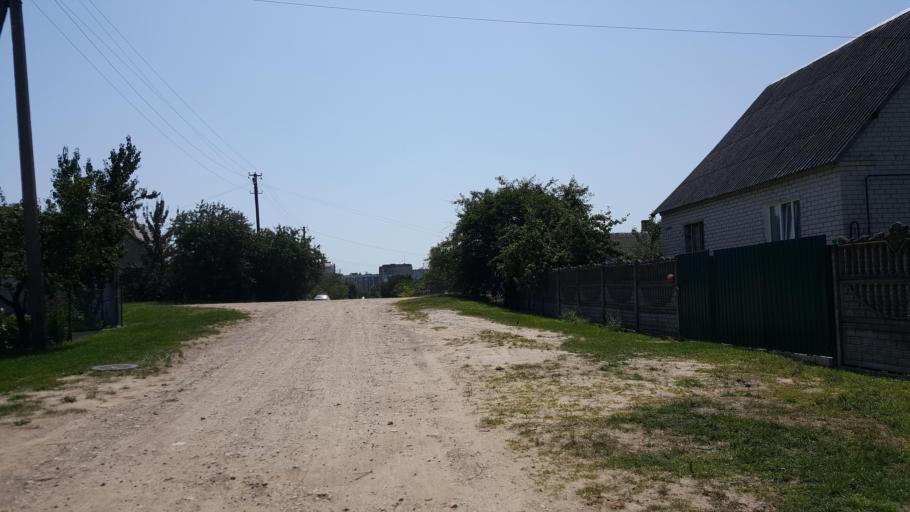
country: BY
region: Brest
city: Zhabinka
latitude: 52.1961
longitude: 23.9810
